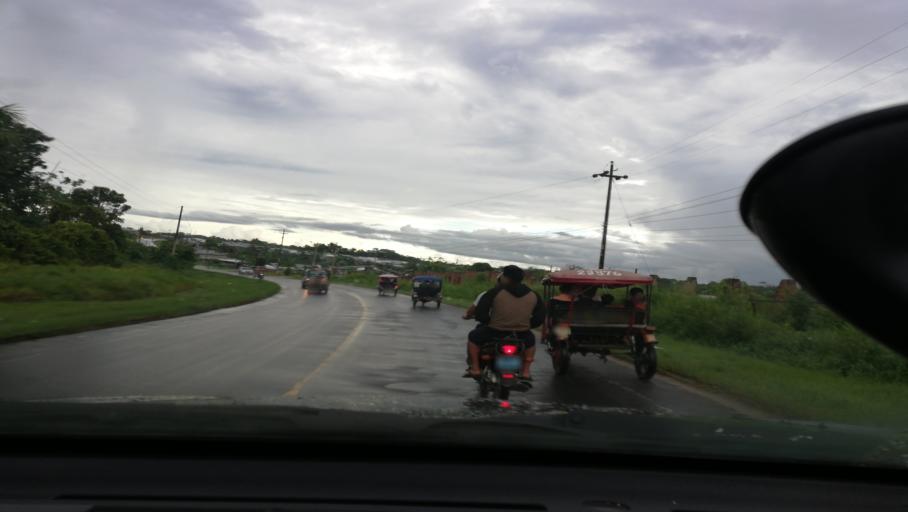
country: PE
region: Loreto
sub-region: Provincia de Maynas
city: Iquitos
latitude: -3.8316
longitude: -73.3285
